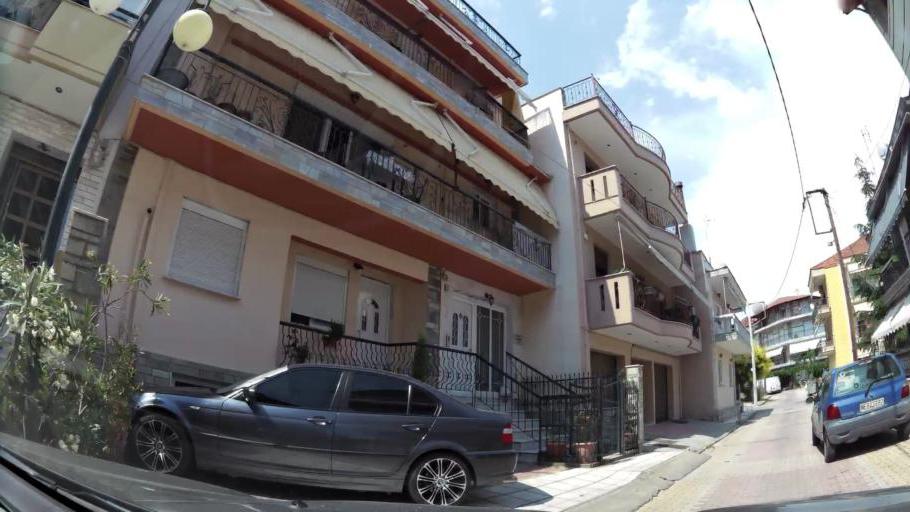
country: GR
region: Central Macedonia
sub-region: Nomos Thessalonikis
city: Stavroupoli
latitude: 40.6764
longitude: 22.9426
